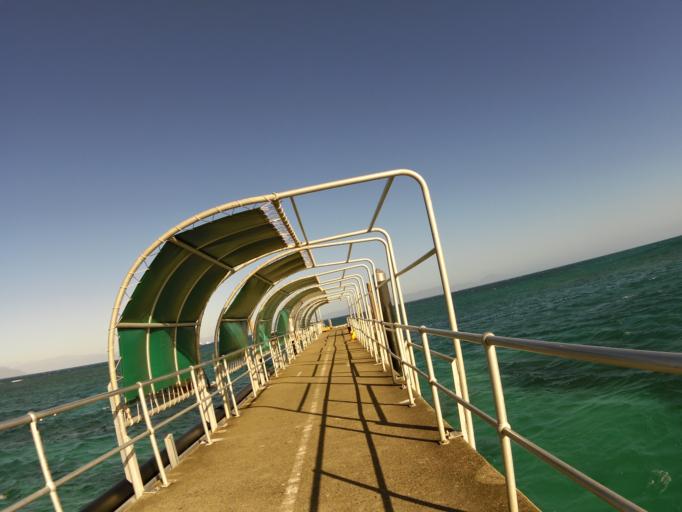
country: AU
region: Queensland
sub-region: Cairns
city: Yorkeys Knob
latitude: -16.7580
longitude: 145.9698
